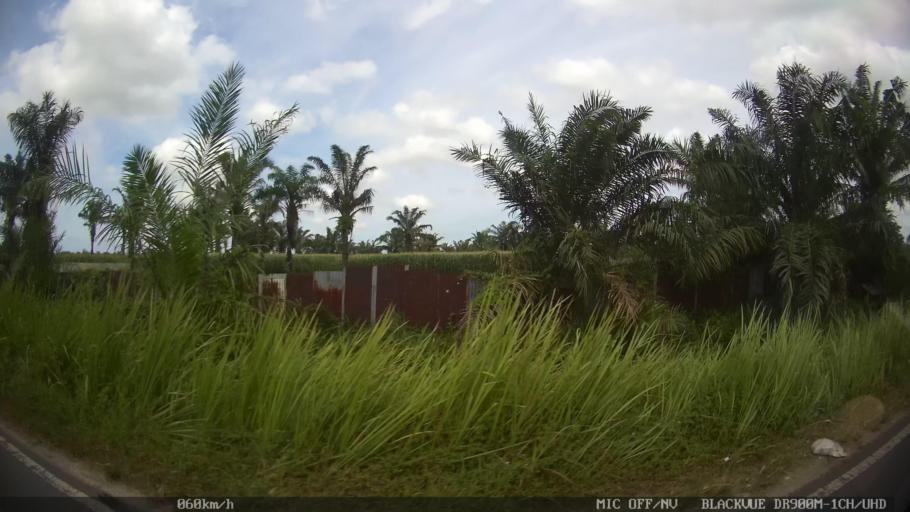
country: ID
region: North Sumatra
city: Percut
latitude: 3.5997
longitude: 98.8386
